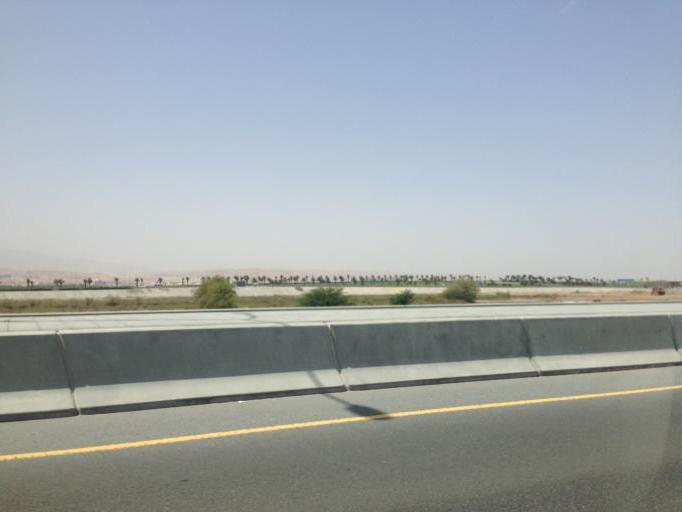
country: OM
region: Muhafazat Masqat
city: Bawshar
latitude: 23.6070
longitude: 58.3181
